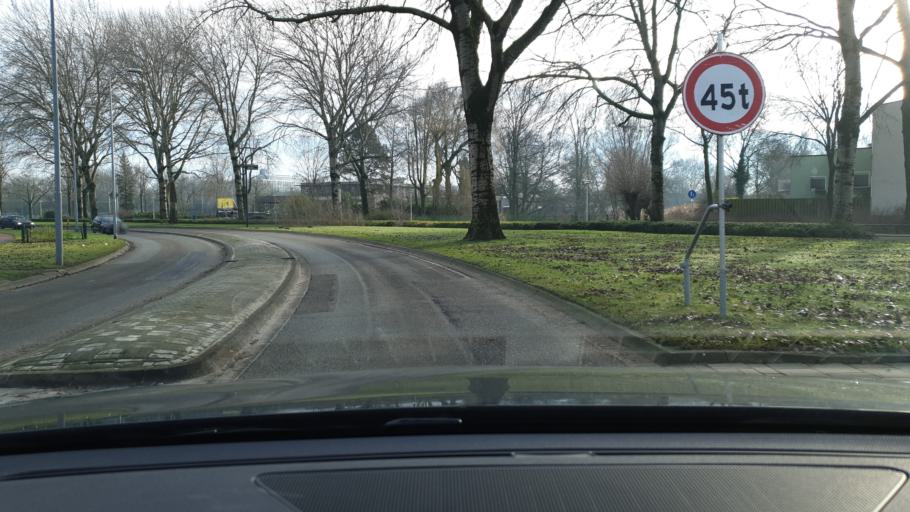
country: NL
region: North Brabant
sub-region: Gemeente Waalre
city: Waalre
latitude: 51.4160
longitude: 5.4467
